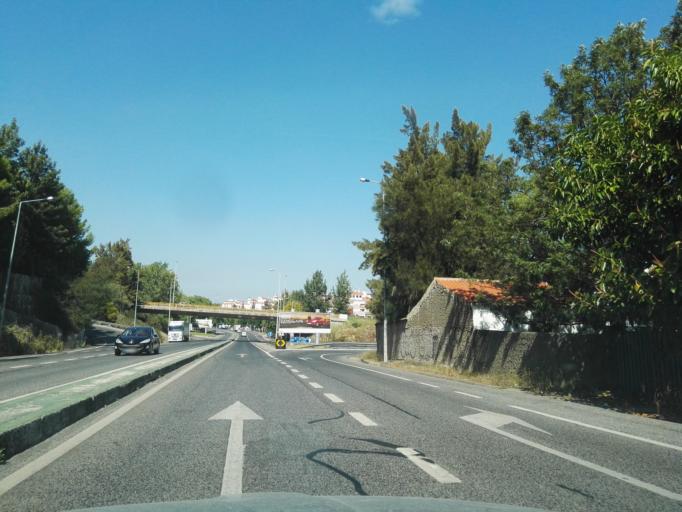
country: PT
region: Lisbon
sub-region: Vila Franca de Xira
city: Vialonga
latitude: 38.8894
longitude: -9.0440
